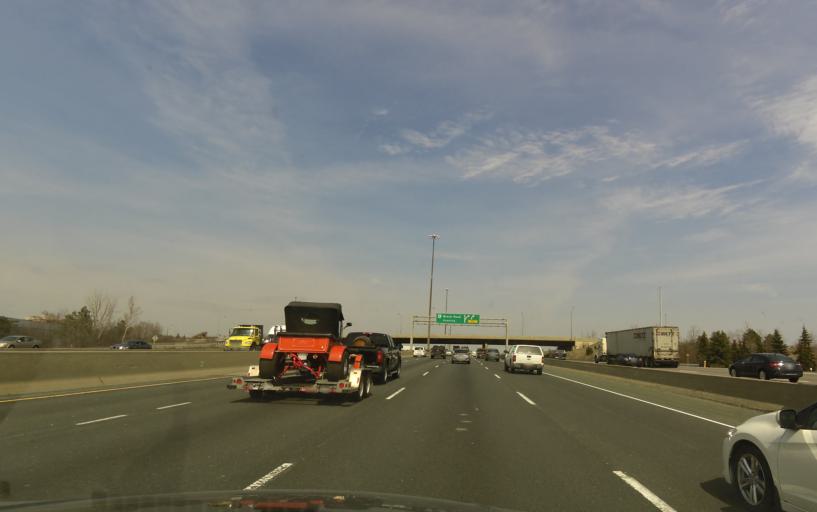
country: CA
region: Ontario
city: Pickering
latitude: 43.8152
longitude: -79.1170
